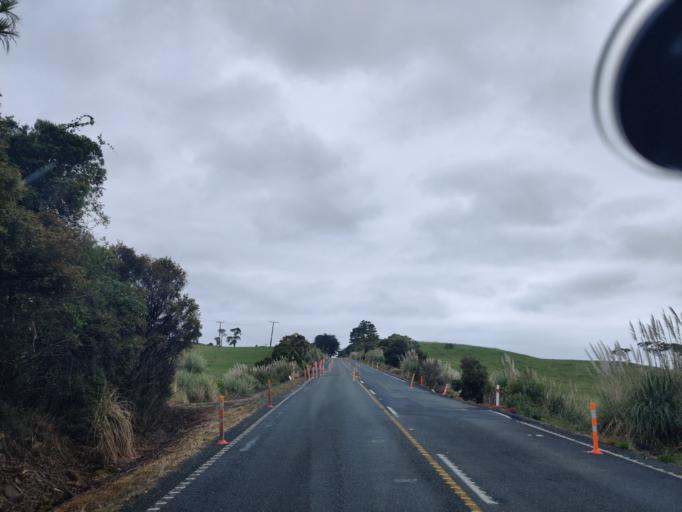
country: NZ
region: Northland
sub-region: Kaipara District
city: Dargaville
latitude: -36.1286
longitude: 174.1316
